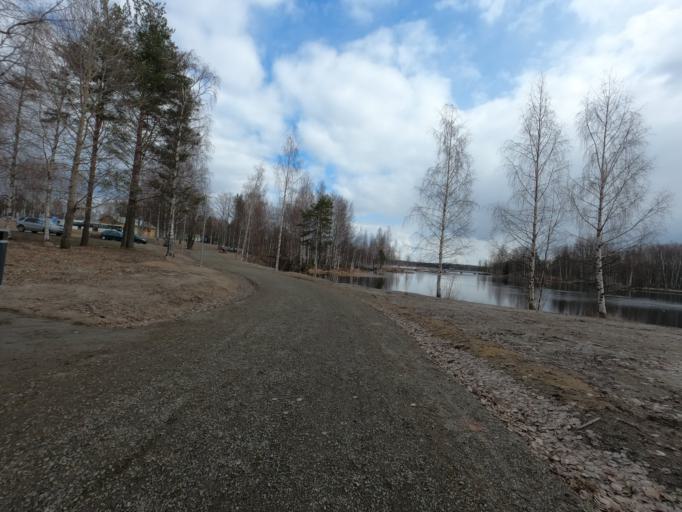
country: FI
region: North Karelia
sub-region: Joensuu
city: Joensuu
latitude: 62.6192
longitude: 29.8660
